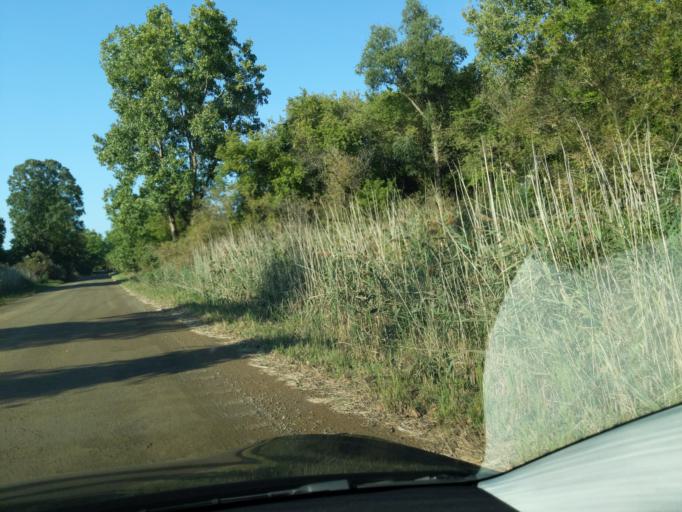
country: US
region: Michigan
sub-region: Oakland County
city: South Lyon
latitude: 42.4565
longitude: -83.6664
